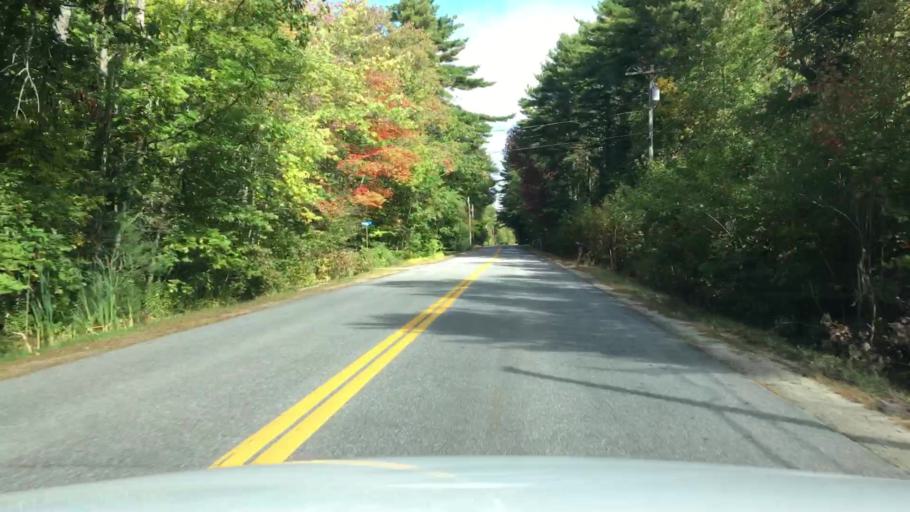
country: US
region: Maine
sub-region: Cumberland County
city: Brunswick
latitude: 43.9437
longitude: -69.8987
